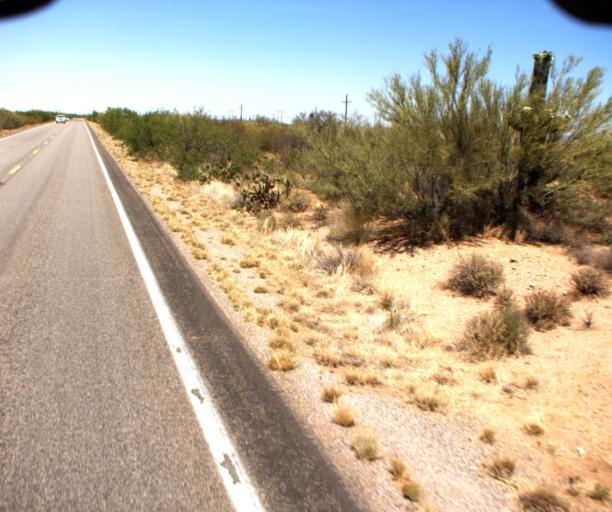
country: US
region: Arizona
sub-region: Pima County
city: Catalina
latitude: 32.7154
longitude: -111.1036
